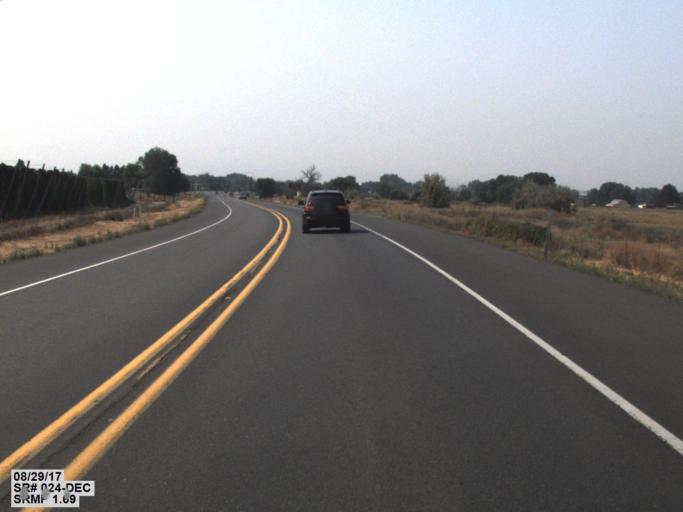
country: US
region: Washington
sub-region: Yakima County
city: Terrace Heights
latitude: 46.5769
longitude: -120.4426
